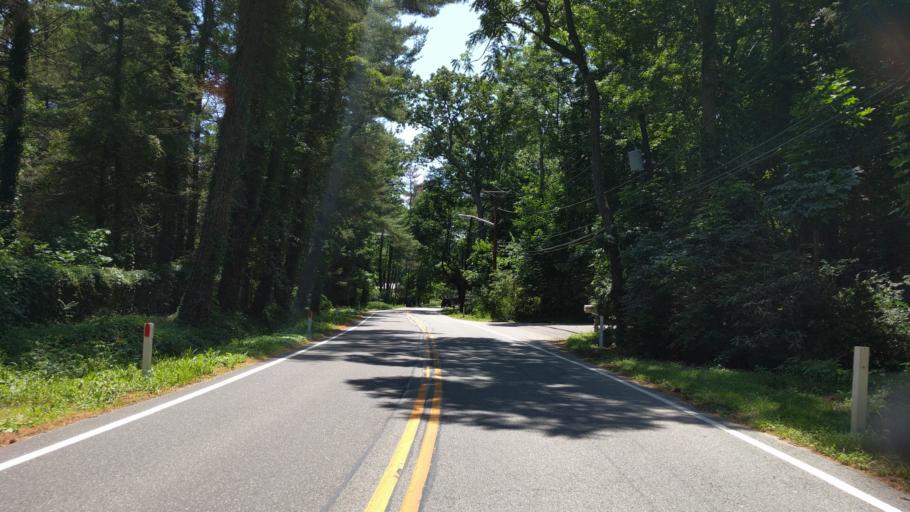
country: US
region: New York
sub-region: Nassau County
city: East Norwich
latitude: 40.8522
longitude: -73.5487
